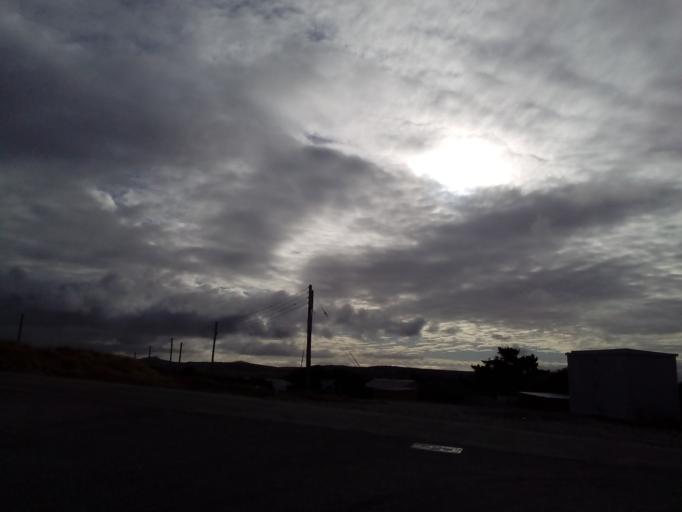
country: FK
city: Stanley
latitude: -51.6920
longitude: -57.8759
